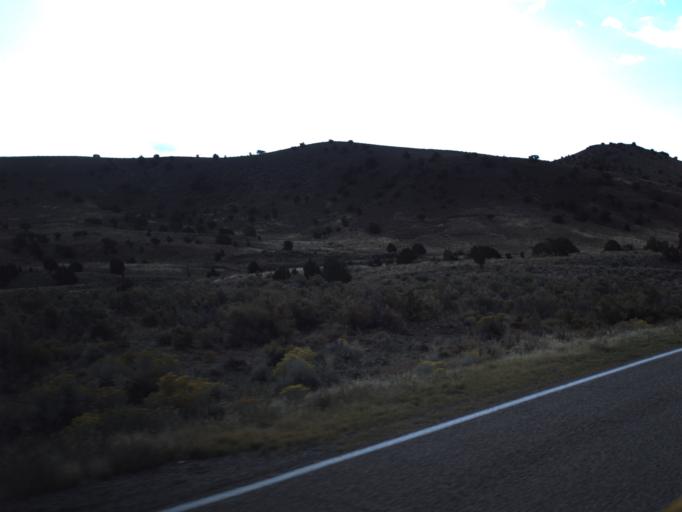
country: US
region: Utah
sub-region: Beaver County
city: Milford
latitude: 38.4526
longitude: -113.2594
